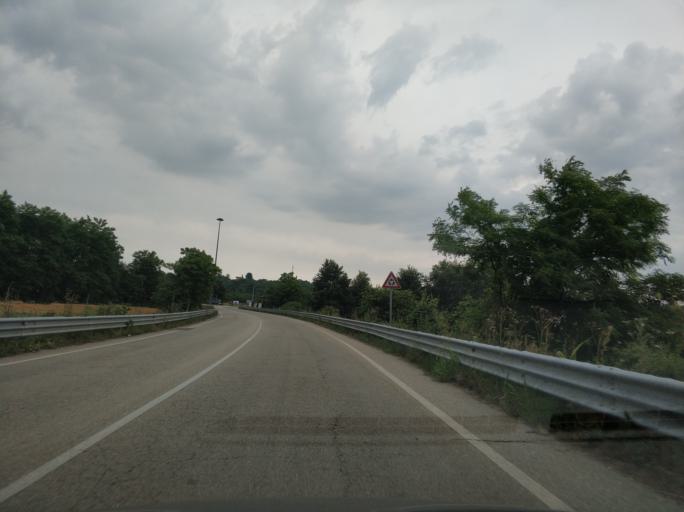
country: IT
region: Piedmont
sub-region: Provincia di Cuneo
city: Monta
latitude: 44.8195
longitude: 7.9483
